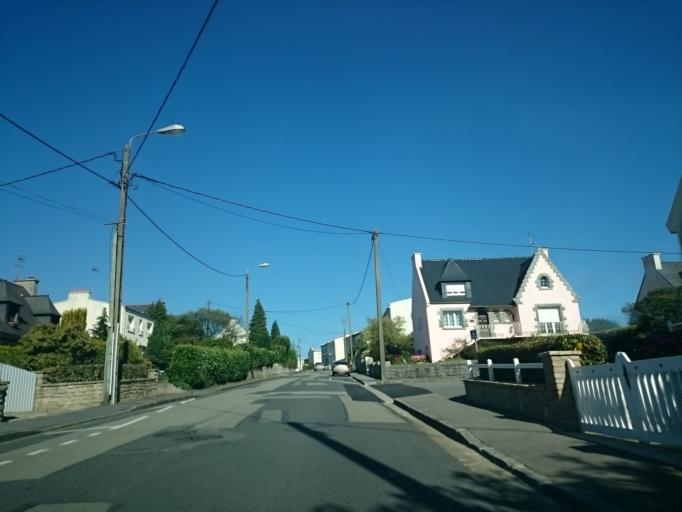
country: FR
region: Brittany
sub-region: Departement du Finistere
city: Gouesnou
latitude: 48.4248
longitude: -4.4647
